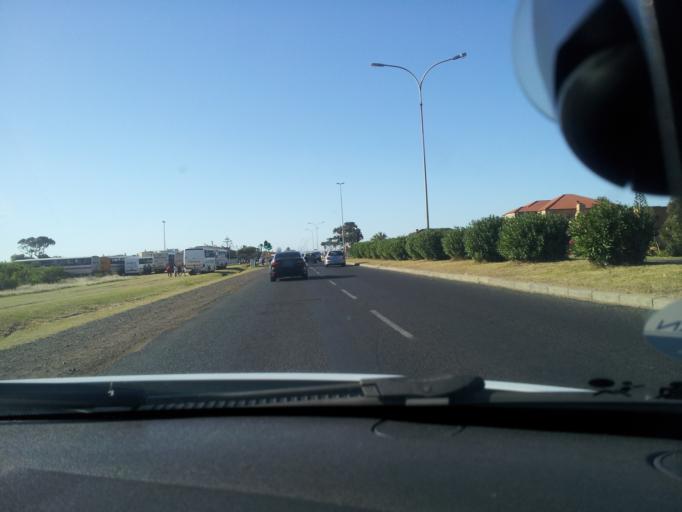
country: ZA
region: Western Cape
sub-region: Overberg District Municipality
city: Grabouw
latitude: -34.1387
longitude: 18.8494
